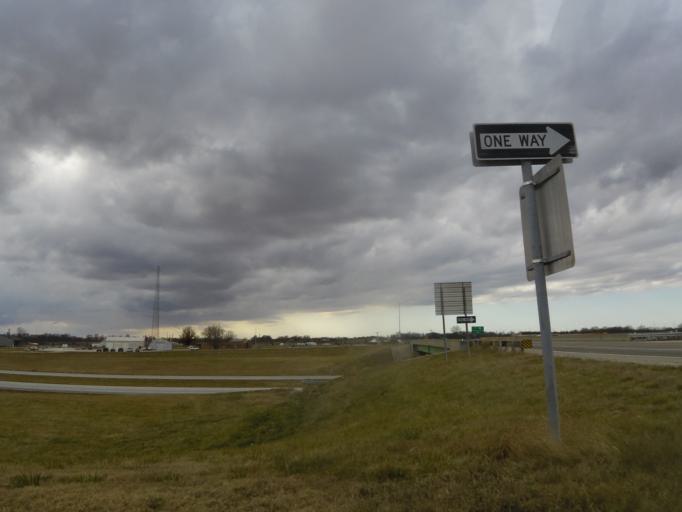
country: US
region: Missouri
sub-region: Ralls County
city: New London
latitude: 39.5745
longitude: -91.3996
